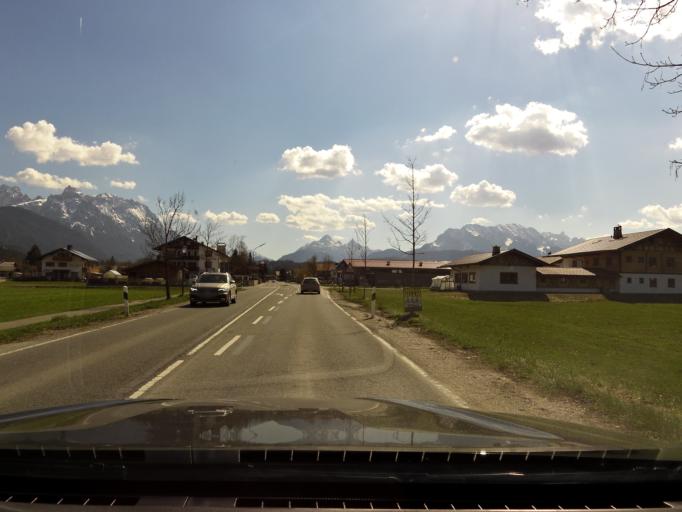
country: DE
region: Bavaria
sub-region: Upper Bavaria
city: Wallgau
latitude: 47.5104
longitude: 11.2794
